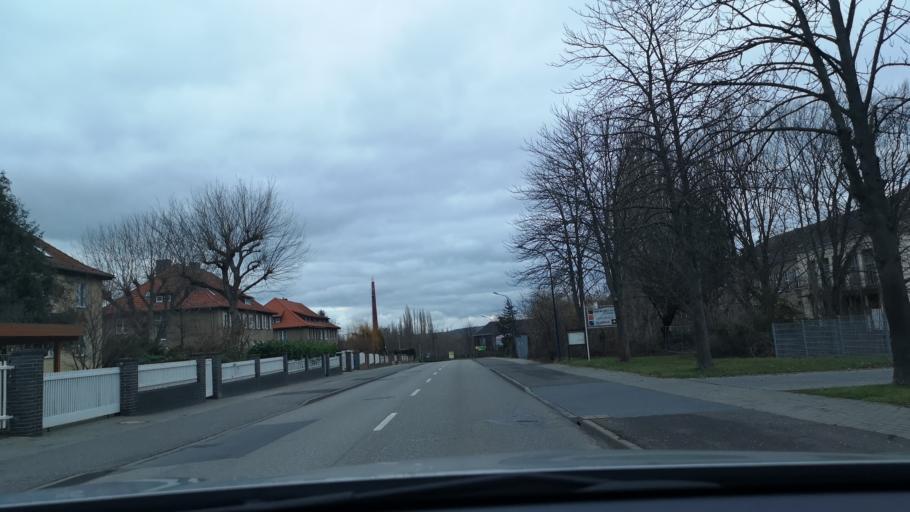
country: DE
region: Saxony-Anhalt
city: Krumpa
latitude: 51.2931
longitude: 11.8538
